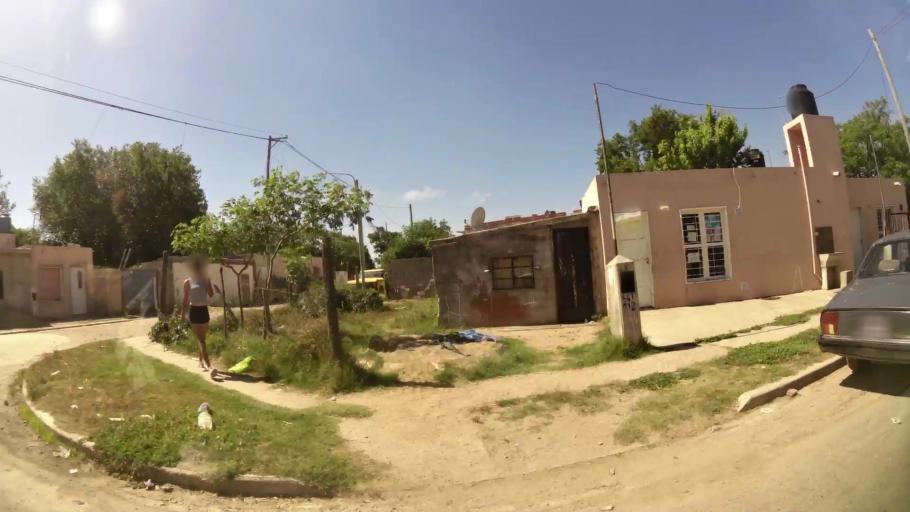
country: AR
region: Cordoba
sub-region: Departamento de Capital
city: Cordoba
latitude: -31.3703
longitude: -64.1602
